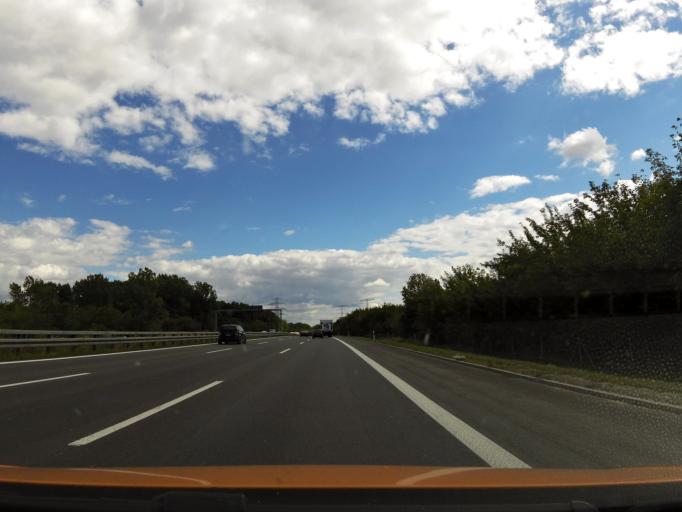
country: DE
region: Berlin
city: Karow
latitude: 52.6293
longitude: 13.4657
